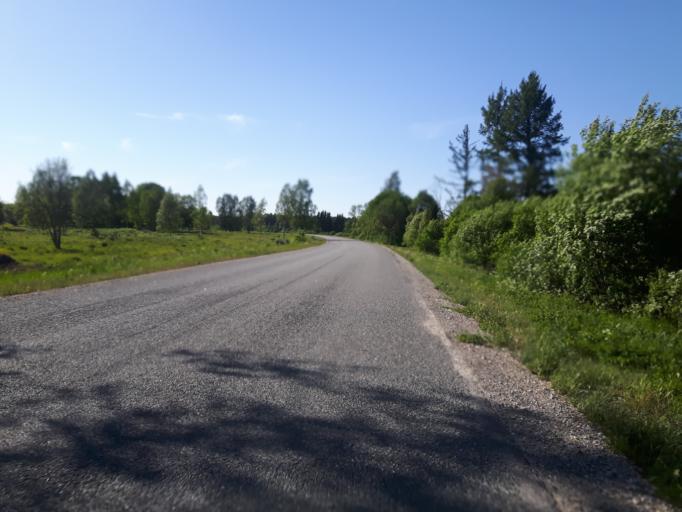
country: EE
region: Laeaene-Virumaa
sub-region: Kadrina vald
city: Kadrina
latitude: 59.5392
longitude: 26.0427
